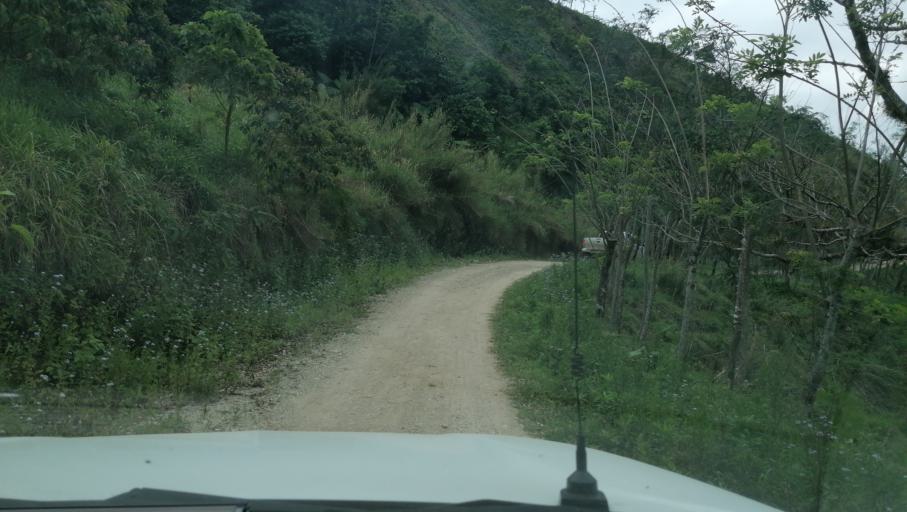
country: MX
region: Chiapas
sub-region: Francisco Leon
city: San Miguel la Sardina
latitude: 17.3451
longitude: -93.3098
